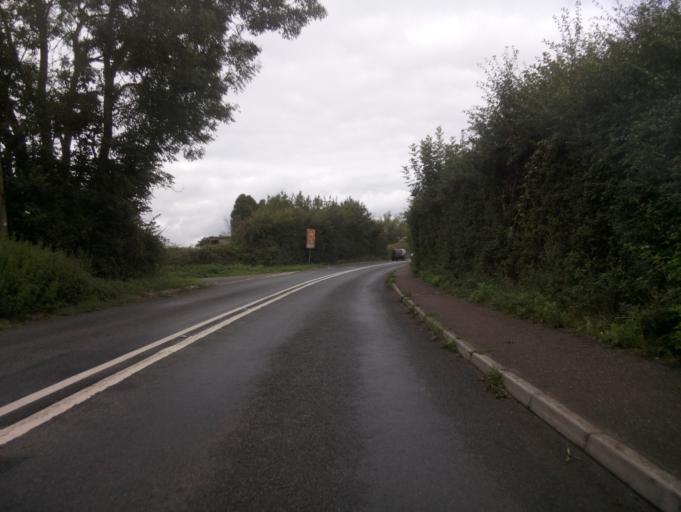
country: GB
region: England
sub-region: Devon
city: Cullompton
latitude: 50.8752
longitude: -3.3871
